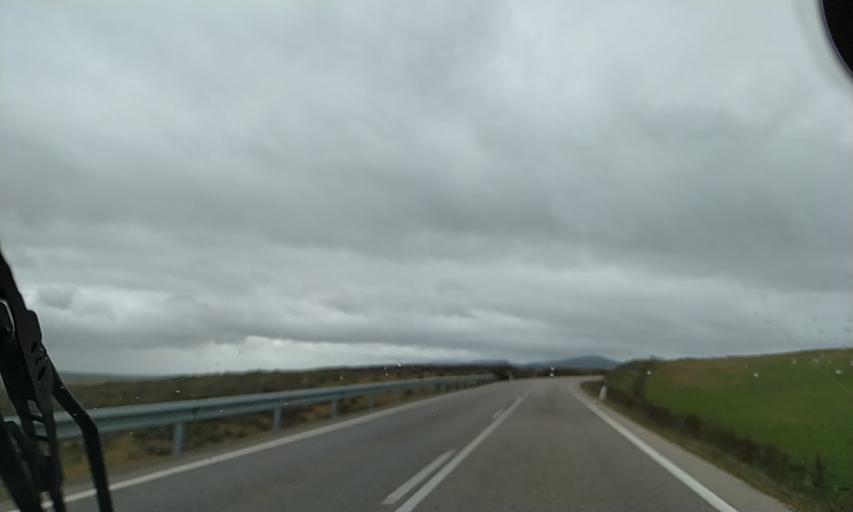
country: ES
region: Extremadura
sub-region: Provincia de Caceres
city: Casar de Caceres
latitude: 39.5262
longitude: -6.3997
